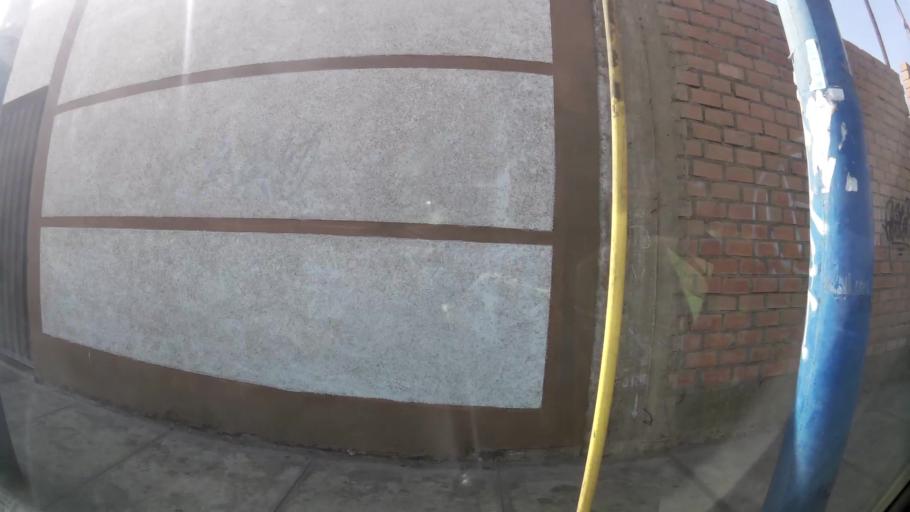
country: PE
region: Lima
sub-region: Huaura
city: Huacho
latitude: -11.1135
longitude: -77.6116
